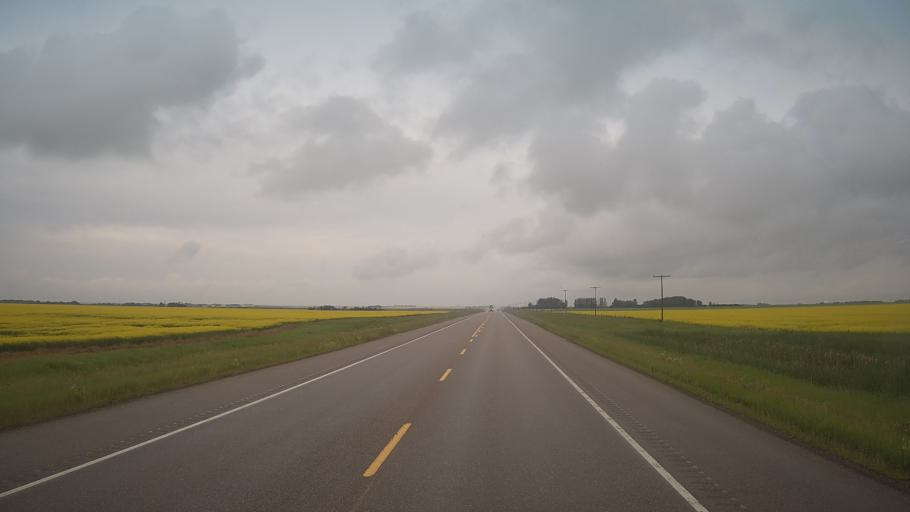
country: CA
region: Saskatchewan
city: Unity
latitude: 52.4349
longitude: -108.9569
